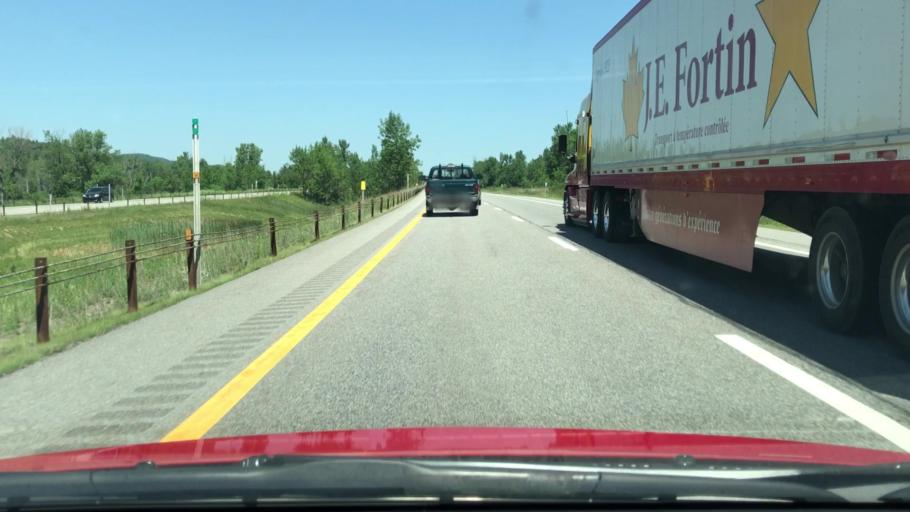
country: US
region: New York
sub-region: Essex County
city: Keeseville
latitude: 44.4311
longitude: -73.4913
